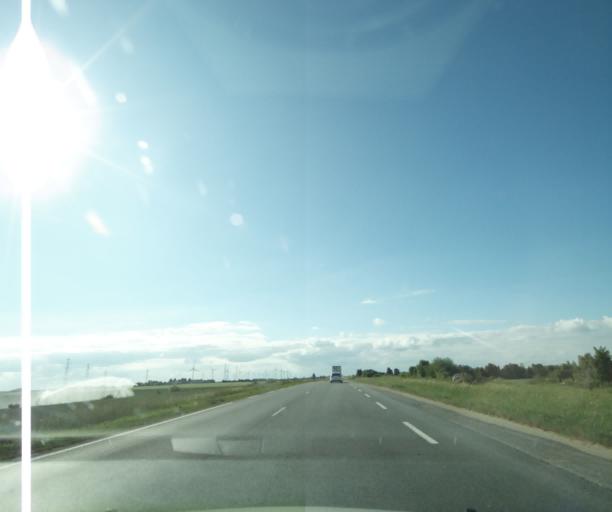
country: FR
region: Centre
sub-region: Departement d'Eure-et-Loir
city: Voves
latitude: 48.2961
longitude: 1.7057
